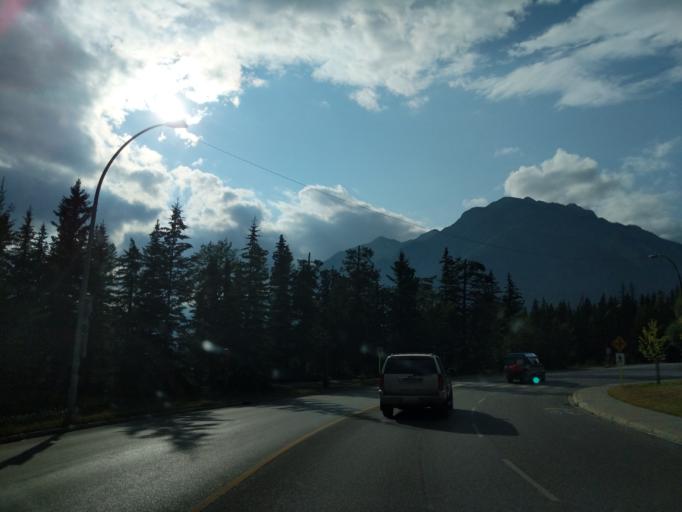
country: CA
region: Alberta
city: Banff
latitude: 51.1802
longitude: -115.5778
